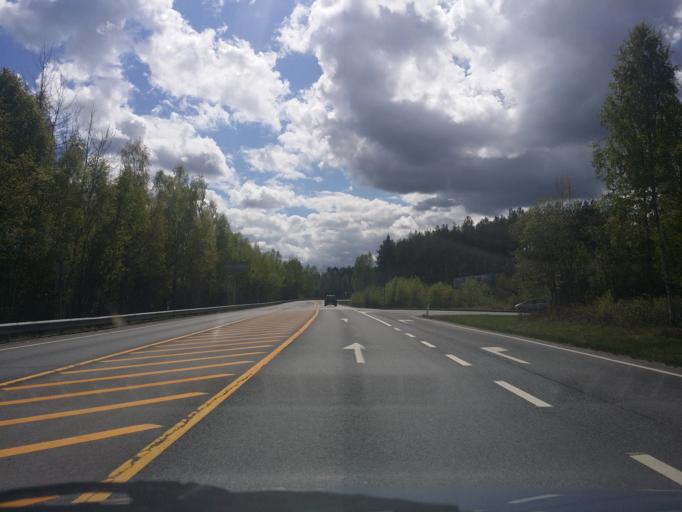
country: NO
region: Buskerud
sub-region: Modum
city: Vikersund
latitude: 59.9450
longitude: 9.9672
